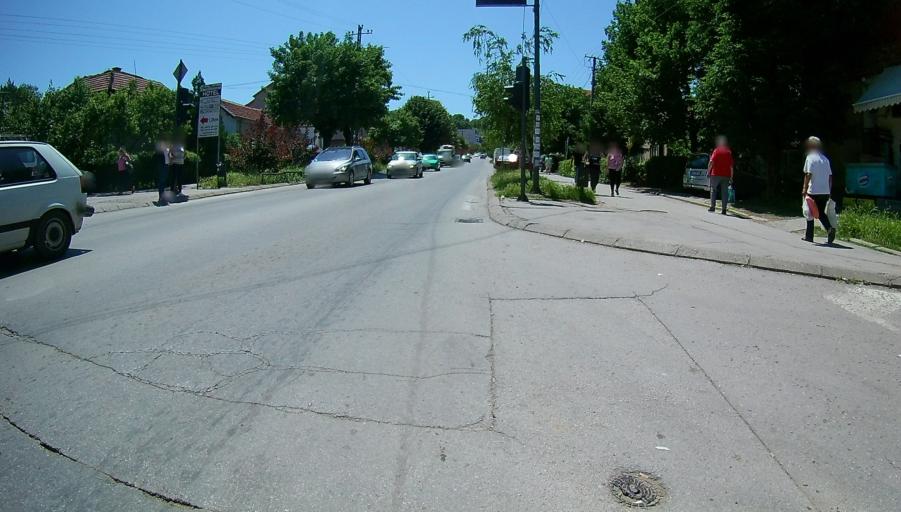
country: RS
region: Central Serbia
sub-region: Nisavski Okrug
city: Nis
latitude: 43.3118
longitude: 21.8766
